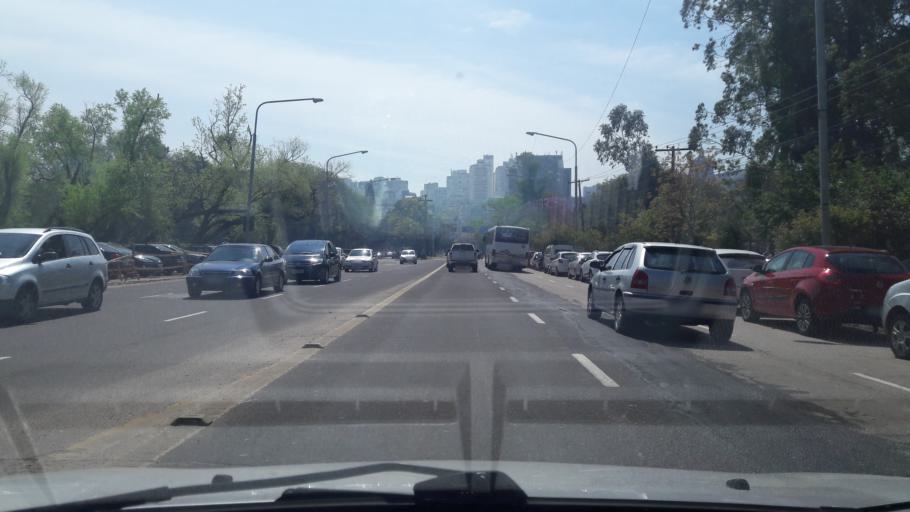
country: BR
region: Rio Grande do Sul
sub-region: Porto Alegre
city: Porto Alegre
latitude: -30.0399
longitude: -51.2329
